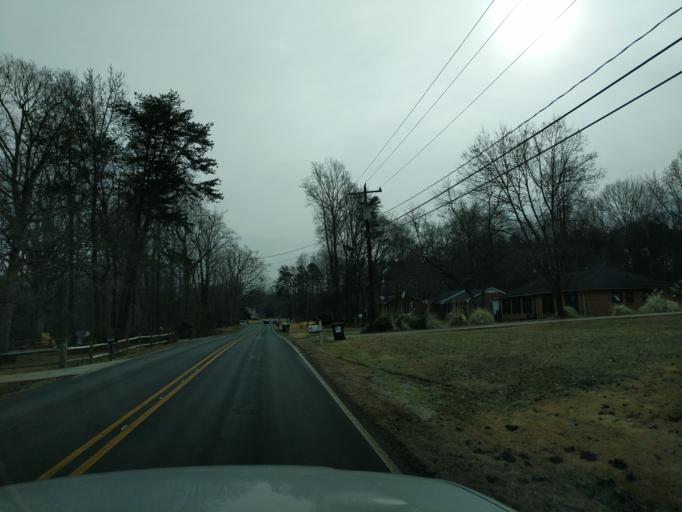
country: US
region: North Carolina
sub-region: Mecklenburg County
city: Charlotte
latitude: 35.3188
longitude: -80.8897
